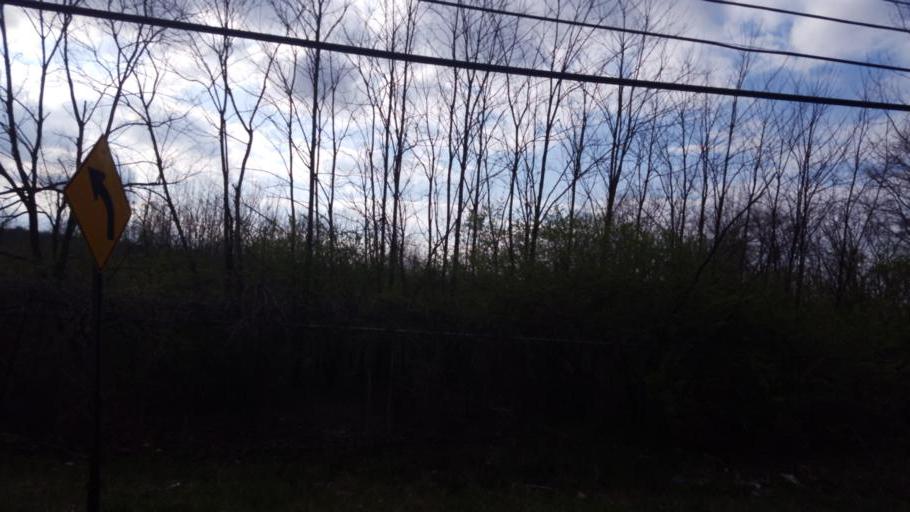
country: US
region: Ohio
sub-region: Delaware County
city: Delaware
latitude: 40.2912
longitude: -83.0545
